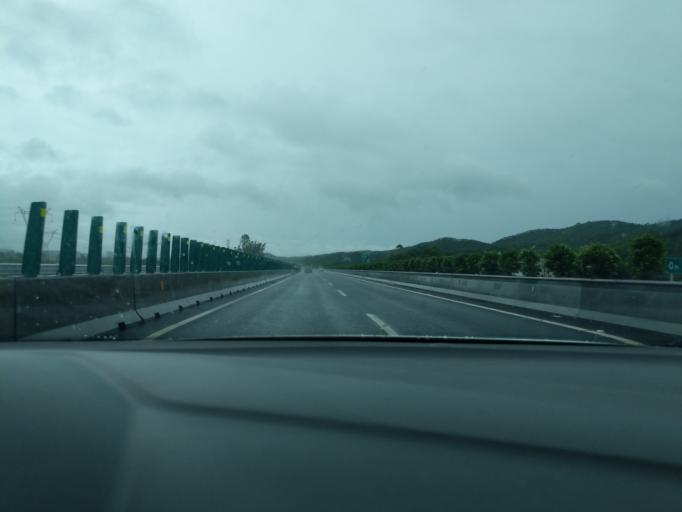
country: CN
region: Guangdong
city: Liangxi
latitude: 22.2685
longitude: 112.3249
